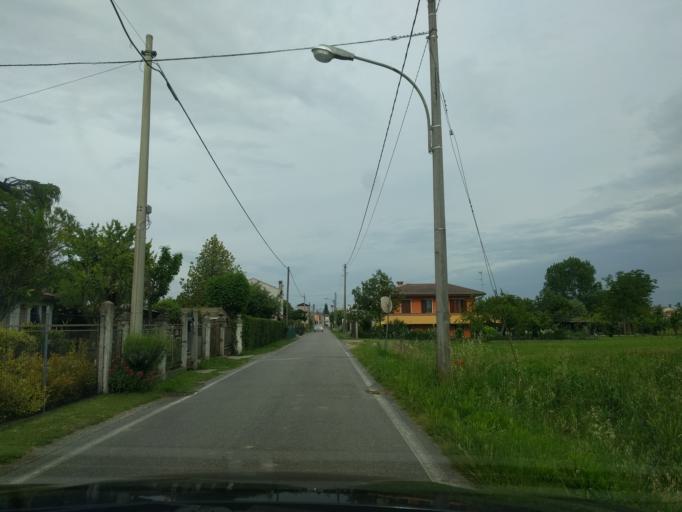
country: IT
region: Veneto
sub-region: Provincia di Rovigo
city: Gavello
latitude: 45.0206
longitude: 11.9105
